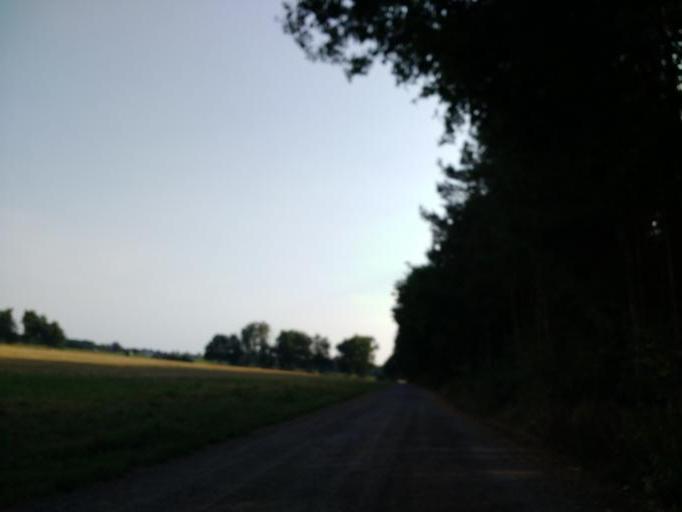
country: DE
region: Lower Saxony
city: Wagenhoff
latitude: 52.5080
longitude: 10.5189
